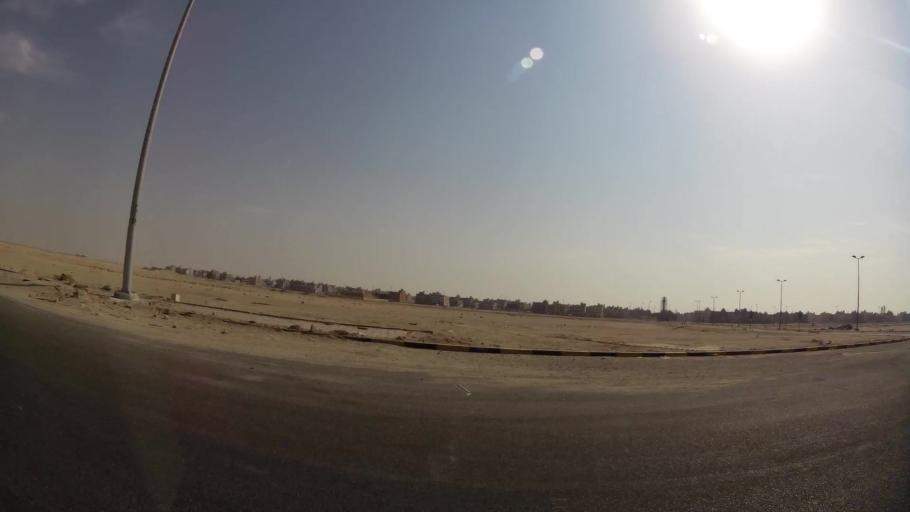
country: KW
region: Al Ahmadi
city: Al Wafrah
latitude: 28.7919
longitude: 48.0771
